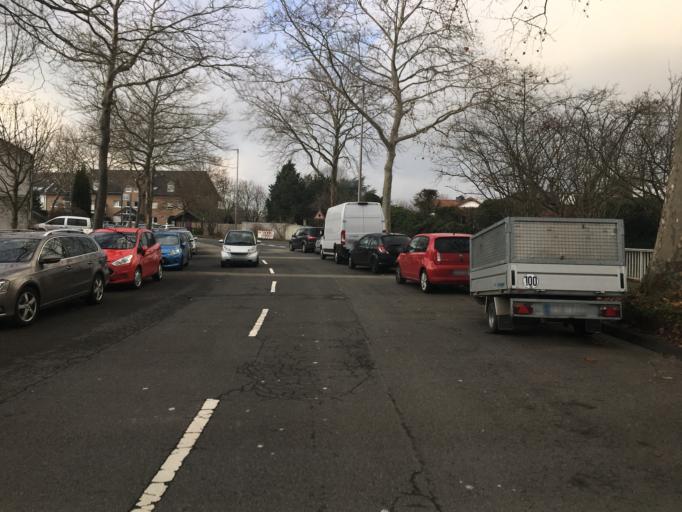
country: DE
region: North Rhine-Westphalia
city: Monheim am Rhein
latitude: 51.0330
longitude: 6.8918
